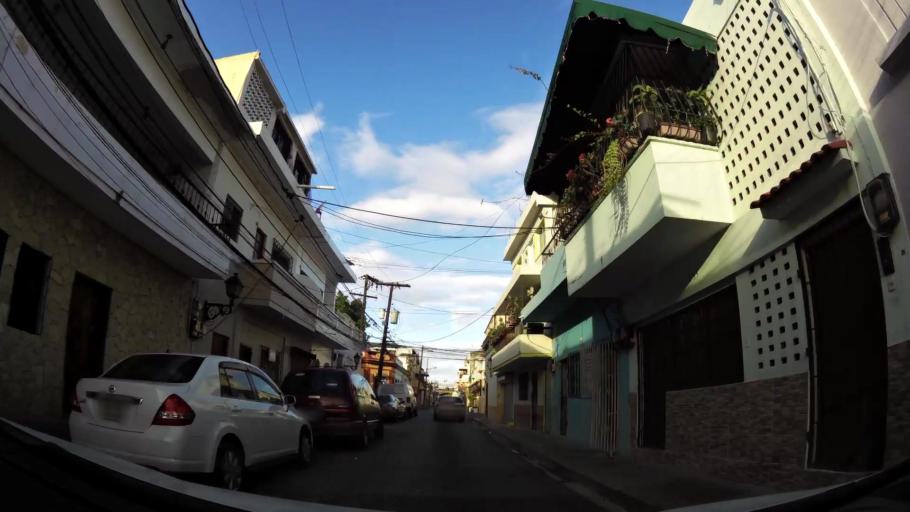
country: DO
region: Nacional
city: Ciudad Nueva
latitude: 18.4690
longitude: -69.8882
